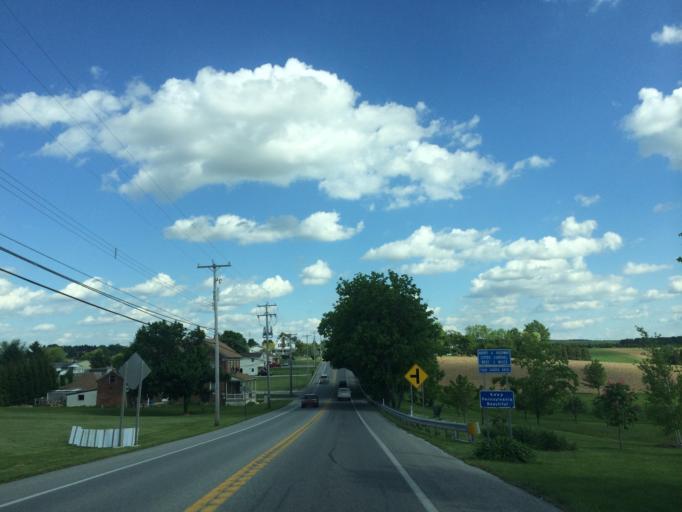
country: US
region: Pennsylvania
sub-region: York County
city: Parkville
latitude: 39.7470
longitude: -76.9484
